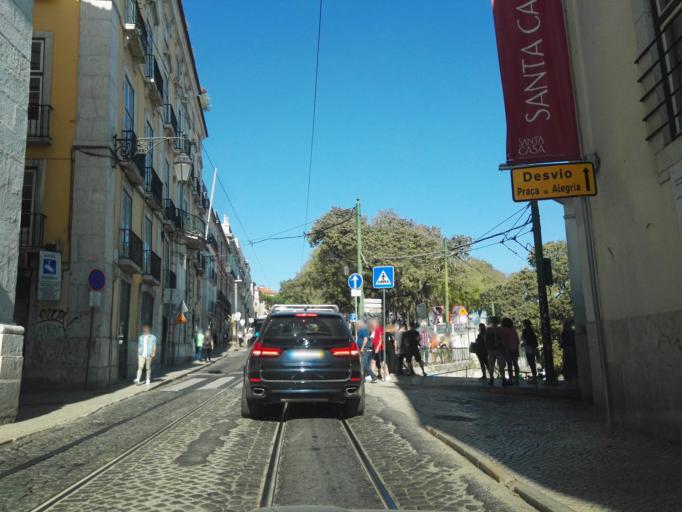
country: PT
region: Lisbon
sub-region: Lisbon
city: Lisbon
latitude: 38.7140
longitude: -9.1439
